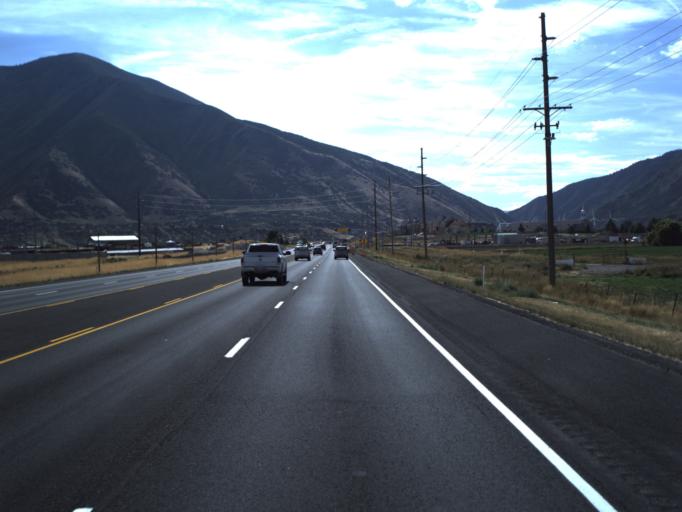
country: US
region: Utah
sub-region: Utah County
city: Spanish Fork
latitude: 40.1014
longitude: -111.6165
